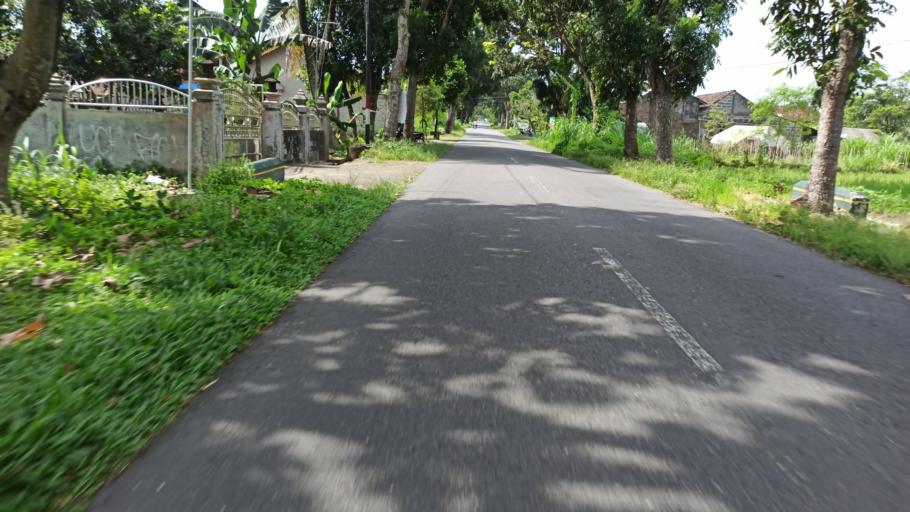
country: ID
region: Daerah Istimewa Yogyakarta
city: Sleman
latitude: -7.6909
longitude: 110.2955
